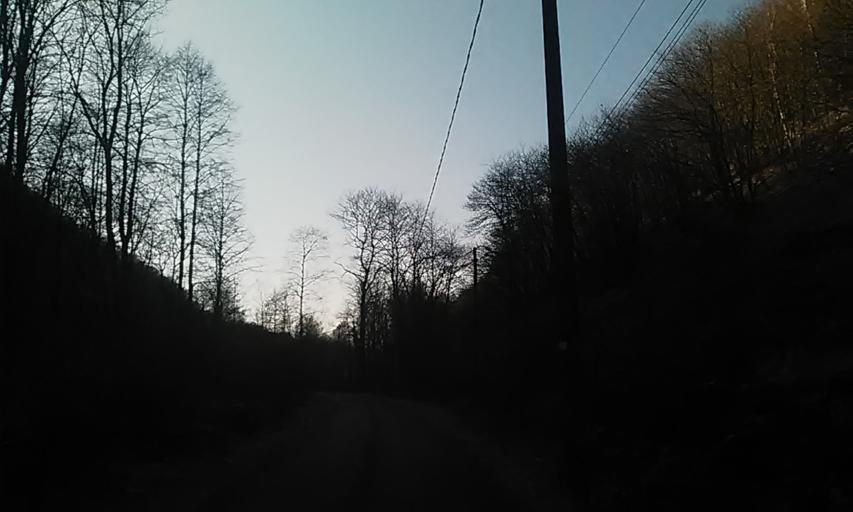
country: IT
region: Piedmont
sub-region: Provincia di Vercelli
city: Quarona
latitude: 45.7727
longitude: 8.2743
